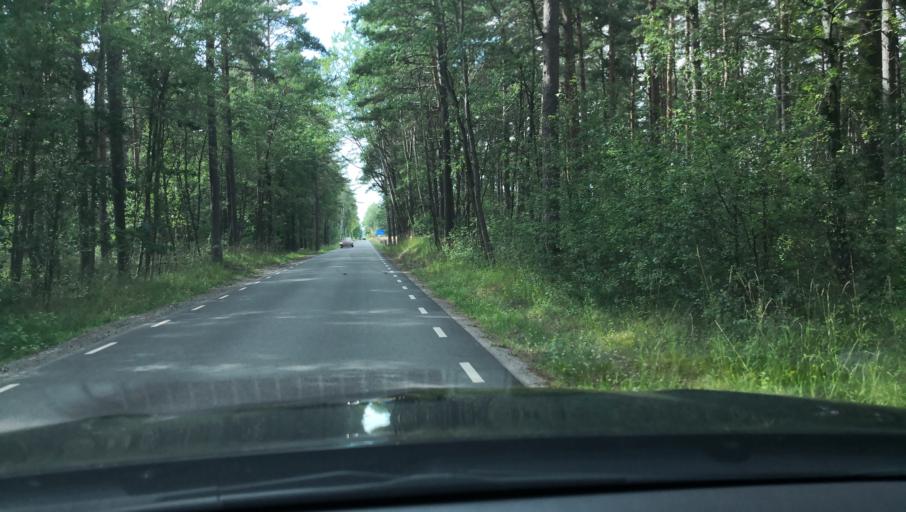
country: SE
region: Skane
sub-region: Simrishamns Kommun
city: Simrishamn
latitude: 55.3923
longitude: 14.1834
